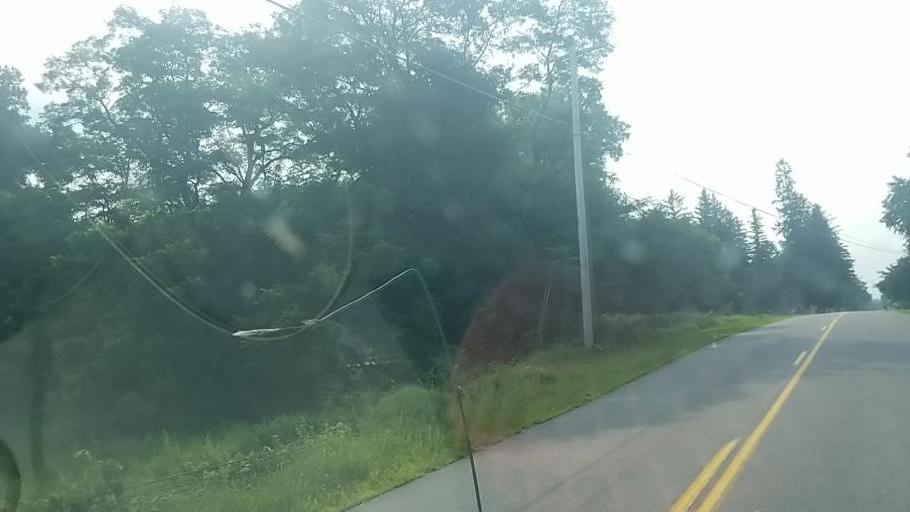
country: US
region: New York
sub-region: Montgomery County
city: Fonda
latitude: 42.9576
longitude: -74.4158
